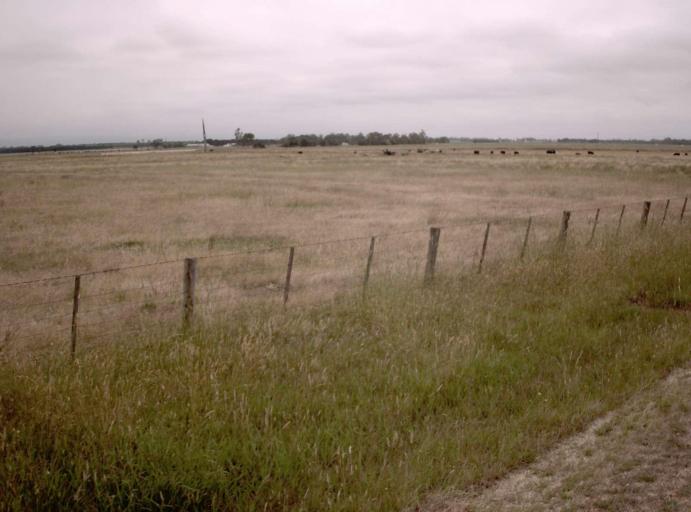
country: AU
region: Victoria
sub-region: Wellington
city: Heyfield
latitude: -38.1049
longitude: 146.7720
